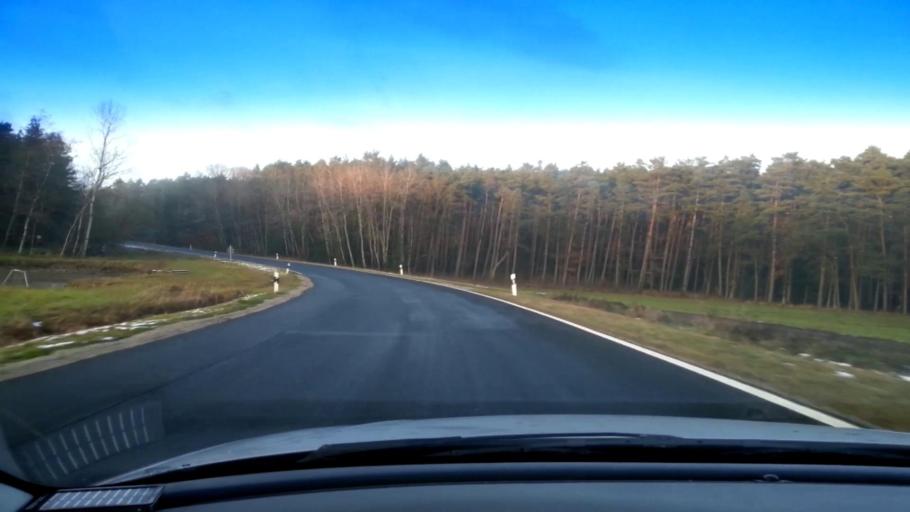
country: DE
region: Bavaria
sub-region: Upper Franconia
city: Frensdorf
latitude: 49.7713
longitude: 10.8950
